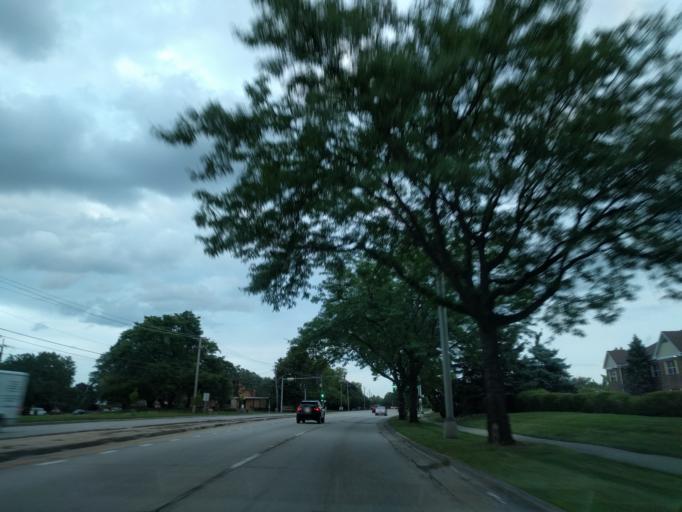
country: US
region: Illinois
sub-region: Cook County
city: Mount Prospect
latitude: 42.0509
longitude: -87.9714
